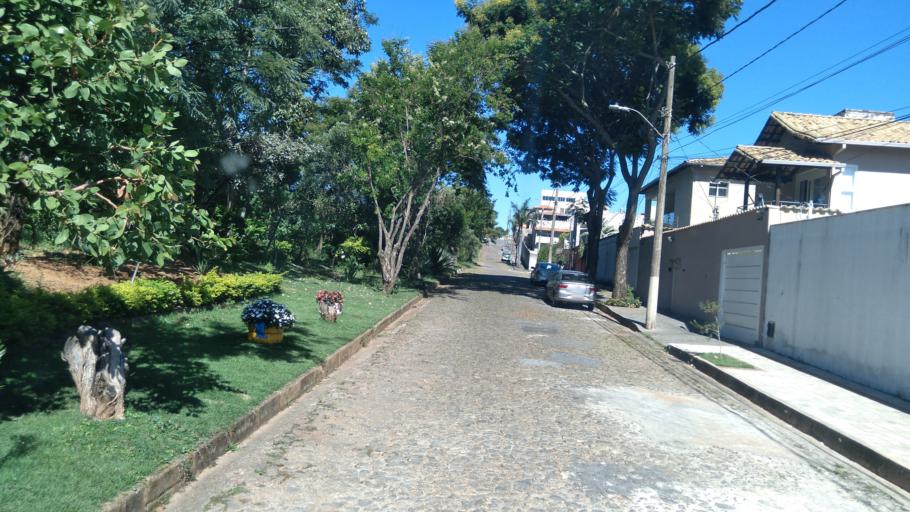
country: BR
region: Minas Gerais
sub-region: Belo Horizonte
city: Belo Horizonte
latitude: -19.9266
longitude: -43.8895
